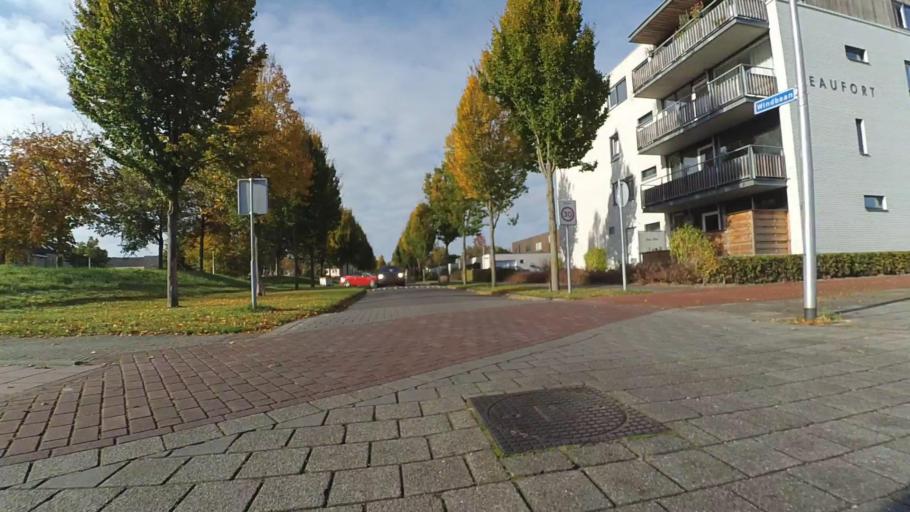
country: NL
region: Flevoland
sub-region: Gemeente Zeewolde
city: Zeewolde
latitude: 52.3330
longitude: 5.5188
